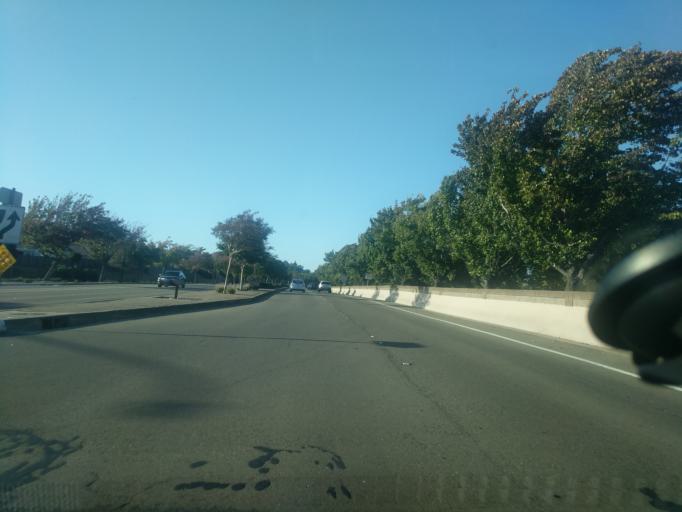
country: US
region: California
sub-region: Alameda County
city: Dublin
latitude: 37.7093
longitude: -121.9377
